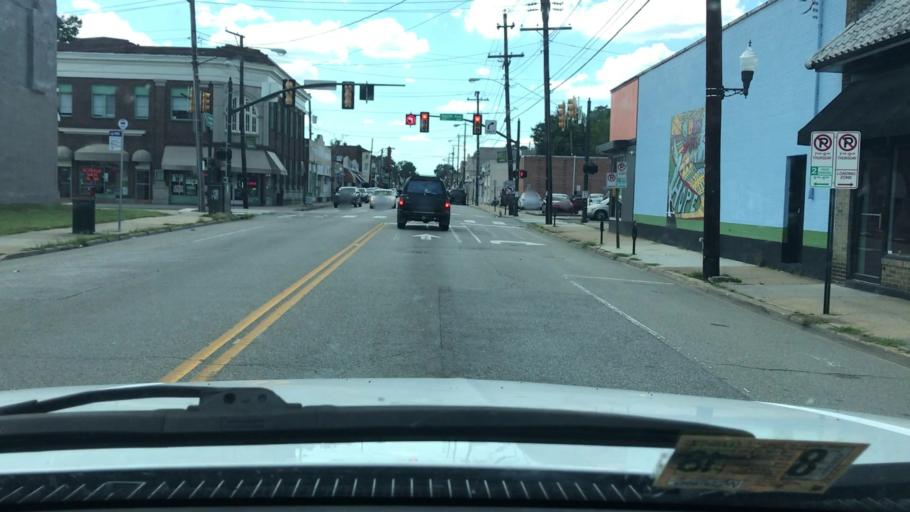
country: US
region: Virginia
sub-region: Henrico County
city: East Highland Park
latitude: 37.5715
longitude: -77.4322
